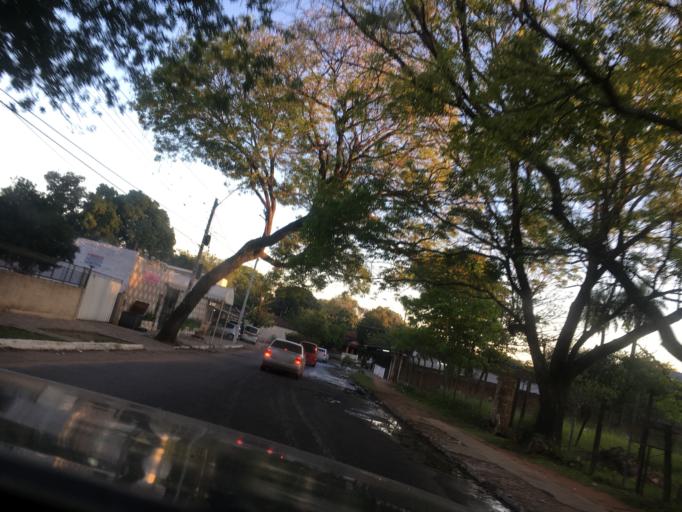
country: PY
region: Central
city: Lambare
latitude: -25.3231
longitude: -57.6111
